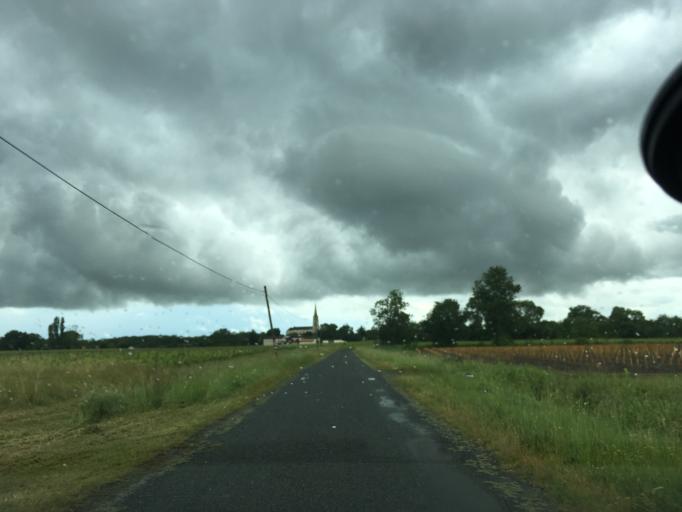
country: FR
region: Aquitaine
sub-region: Departement de la Gironde
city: Saint-Estephe
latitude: 45.3275
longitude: -0.8167
